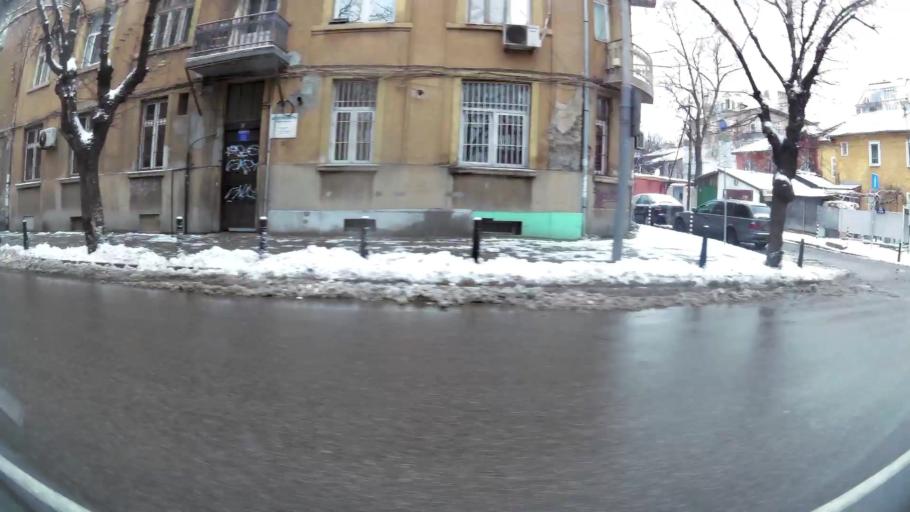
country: BG
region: Sofia-Capital
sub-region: Stolichna Obshtina
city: Sofia
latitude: 42.7068
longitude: 23.3282
